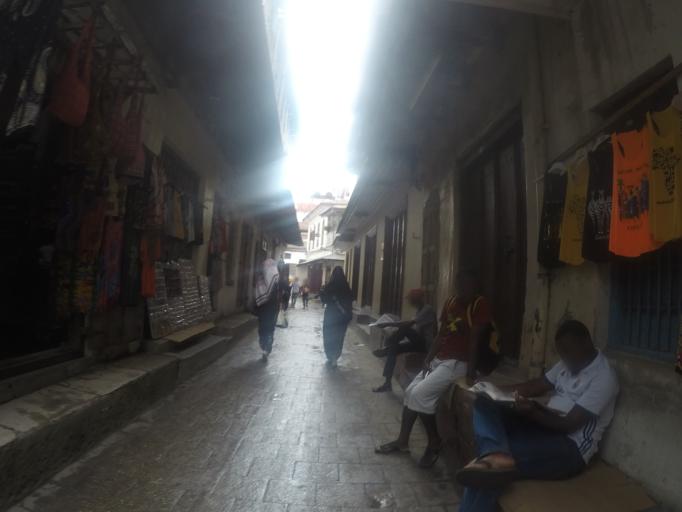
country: TZ
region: Zanzibar Urban/West
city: Zanzibar
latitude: -6.1623
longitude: 39.1922
